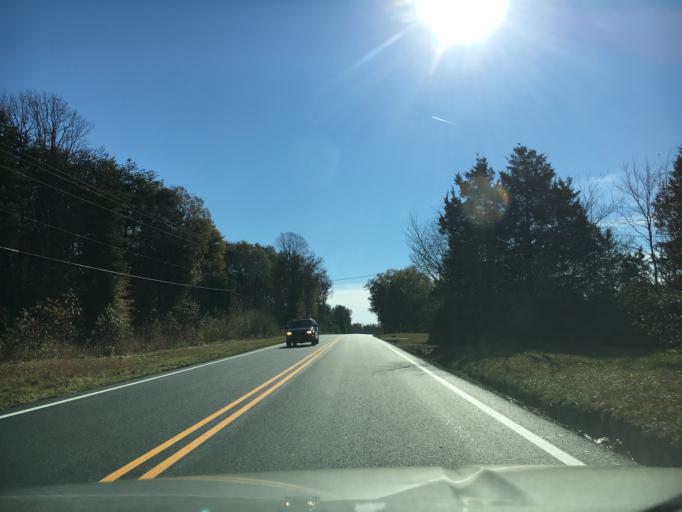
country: US
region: Virginia
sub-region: Cumberland County
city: Cumberland
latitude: 37.4719
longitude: -78.2815
